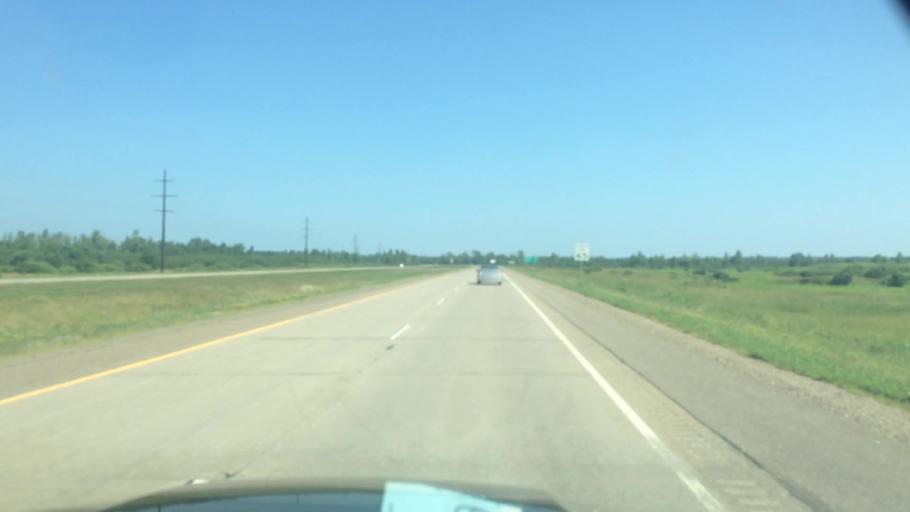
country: US
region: Wisconsin
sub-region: Lincoln County
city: Merrill
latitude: 45.2212
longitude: -89.6707
